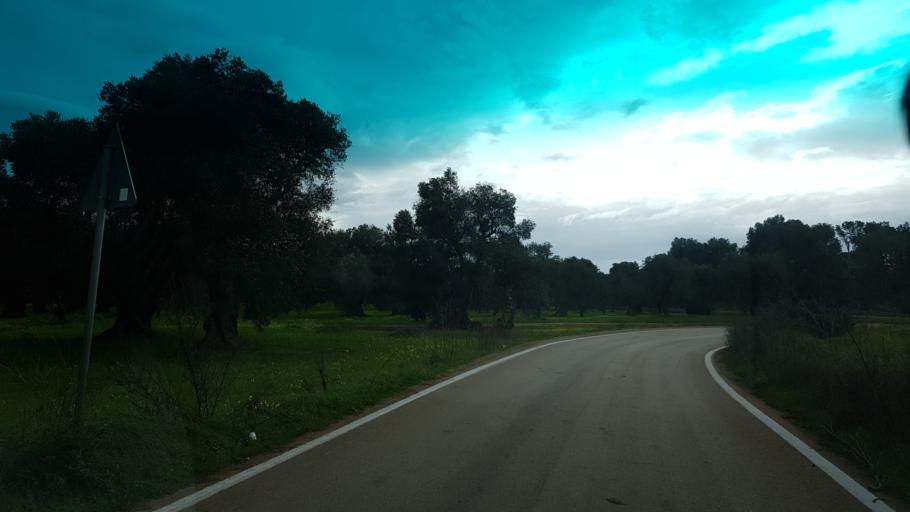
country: IT
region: Apulia
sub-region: Provincia di Brindisi
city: San Vito dei Normanni
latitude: 40.7010
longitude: 17.7639
